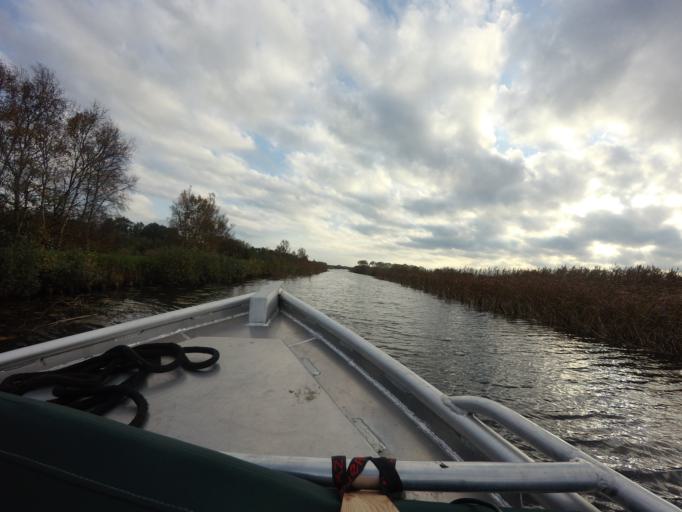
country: NL
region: Overijssel
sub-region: Gemeente Steenwijkerland
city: Blokzijl
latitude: 52.7424
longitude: 5.9750
